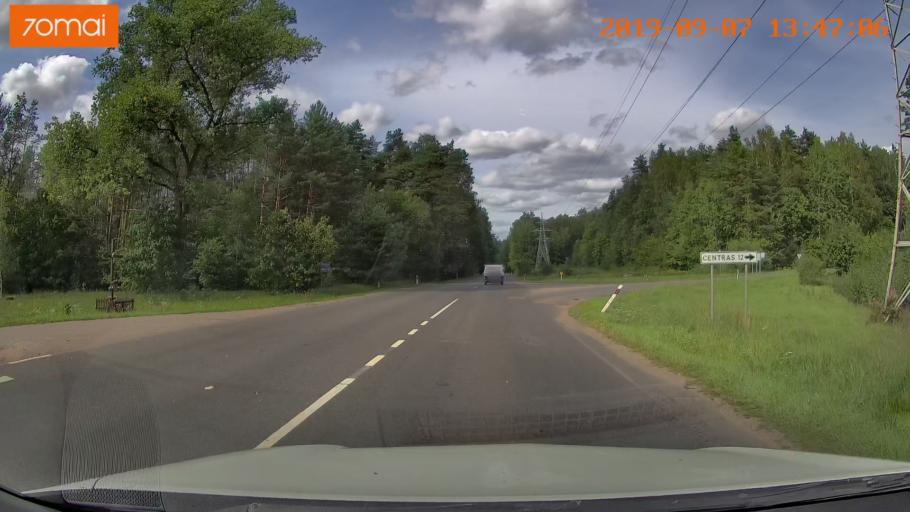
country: LT
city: Baltoji Voke
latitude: 54.5945
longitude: 25.2188
